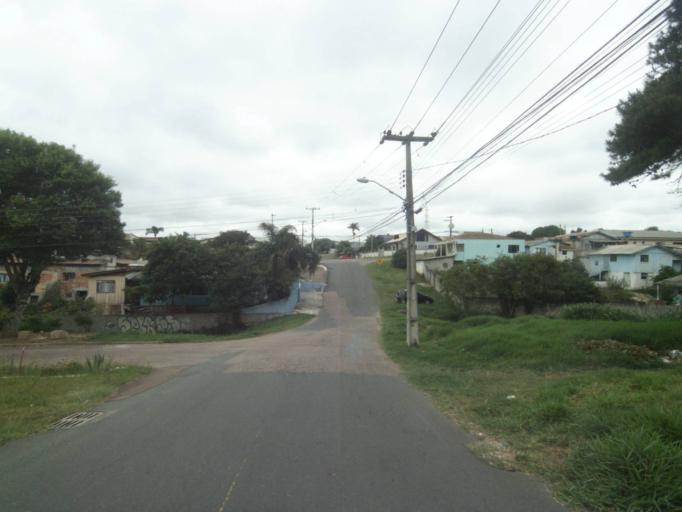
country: BR
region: Parana
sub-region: Sao Jose Dos Pinhais
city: Sao Jose dos Pinhais
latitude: -25.5436
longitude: -49.2896
